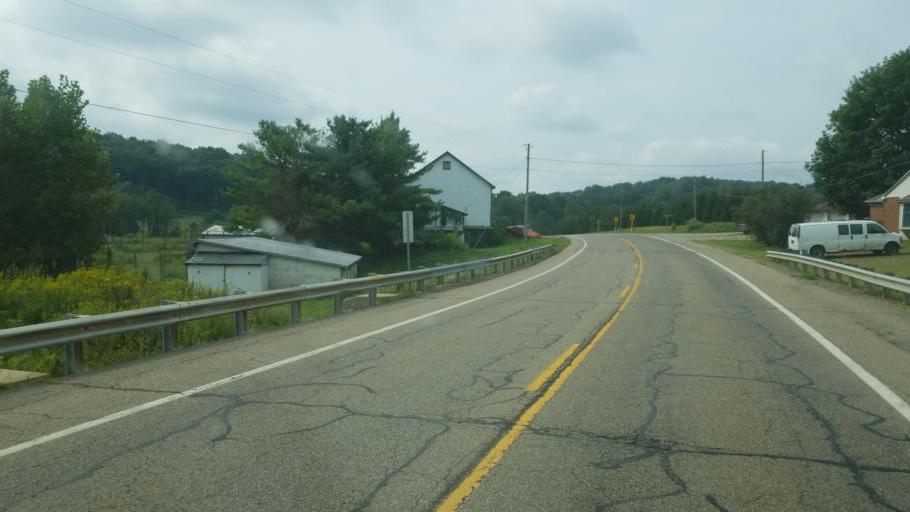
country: US
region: Ohio
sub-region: Knox County
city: Danville
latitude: 40.5162
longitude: -82.3254
